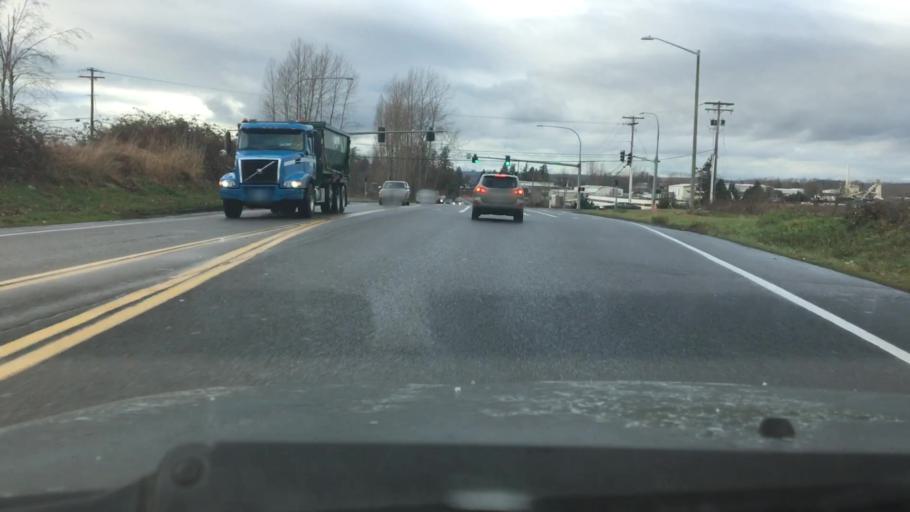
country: US
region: Washington
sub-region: Whatcom County
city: Marietta-Alderwood
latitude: 48.8173
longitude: -122.5534
